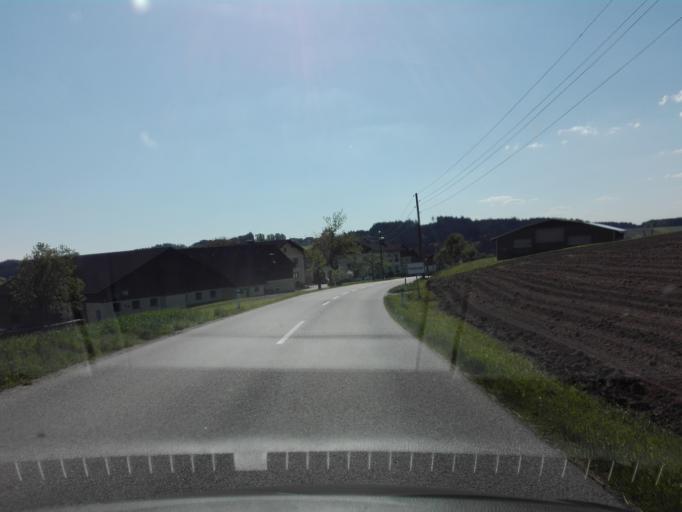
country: DE
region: Bavaria
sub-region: Lower Bavaria
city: Obernzell
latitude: 48.4579
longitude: 13.6135
